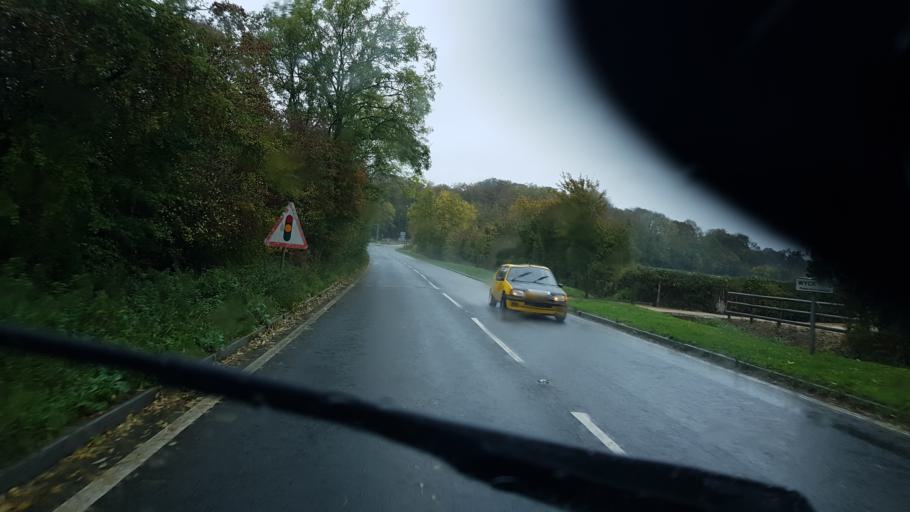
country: GB
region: England
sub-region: Gloucestershire
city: Stow on the Wold
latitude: 51.9159
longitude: -1.7240
